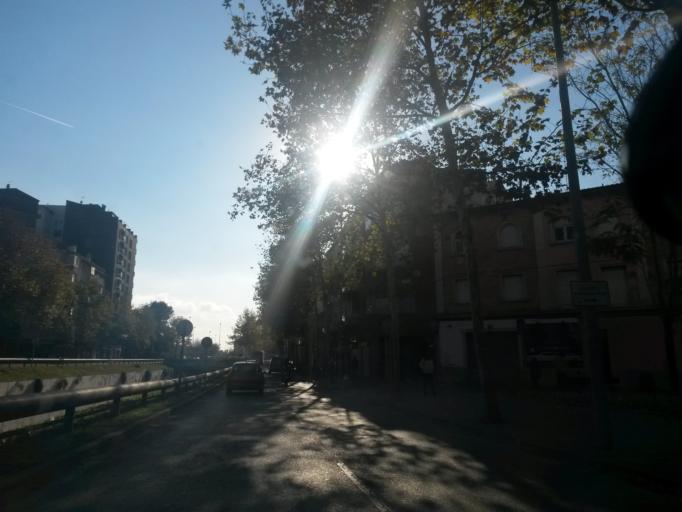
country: ES
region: Catalonia
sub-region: Provincia de Girona
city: Girona
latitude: 41.9781
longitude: 2.8104
